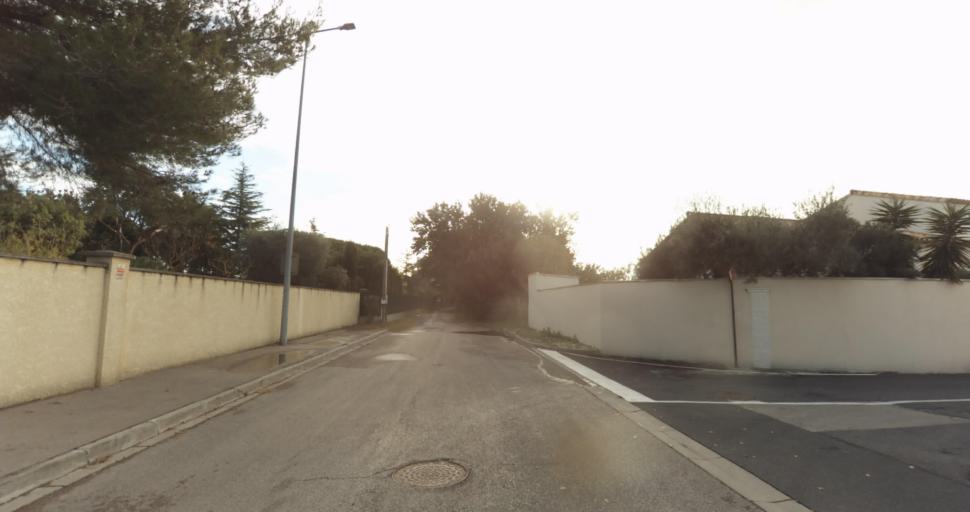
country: FR
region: Languedoc-Roussillon
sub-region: Departement du Gard
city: Aigues-Mortes
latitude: 43.5627
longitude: 4.2070
